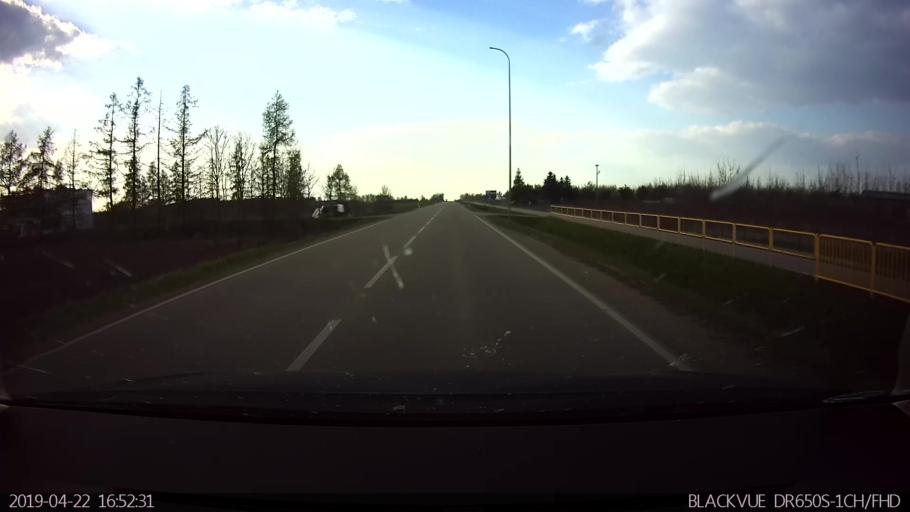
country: PL
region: Podlasie
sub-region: Powiat siemiatycki
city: Siemiatycze
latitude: 52.4439
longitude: 22.8467
